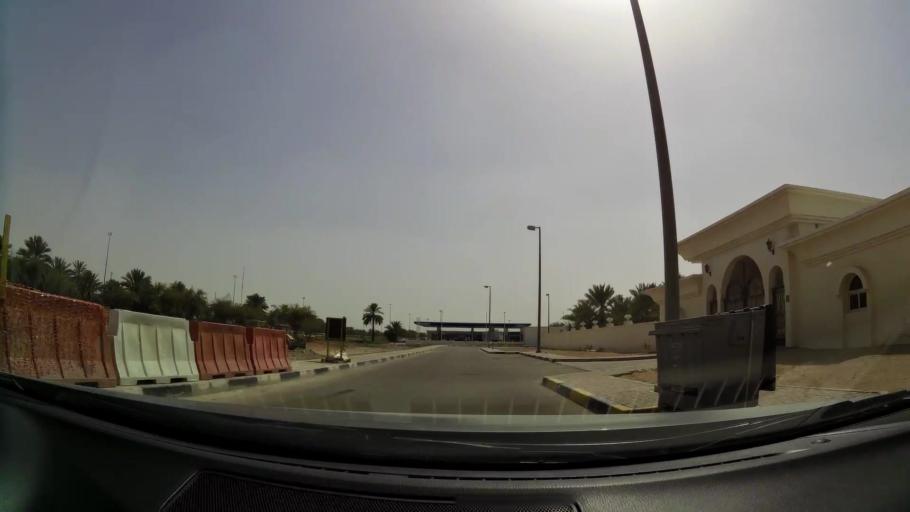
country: AE
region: Abu Dhabi
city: Al Ain
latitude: 24.2187
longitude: 55.6857
